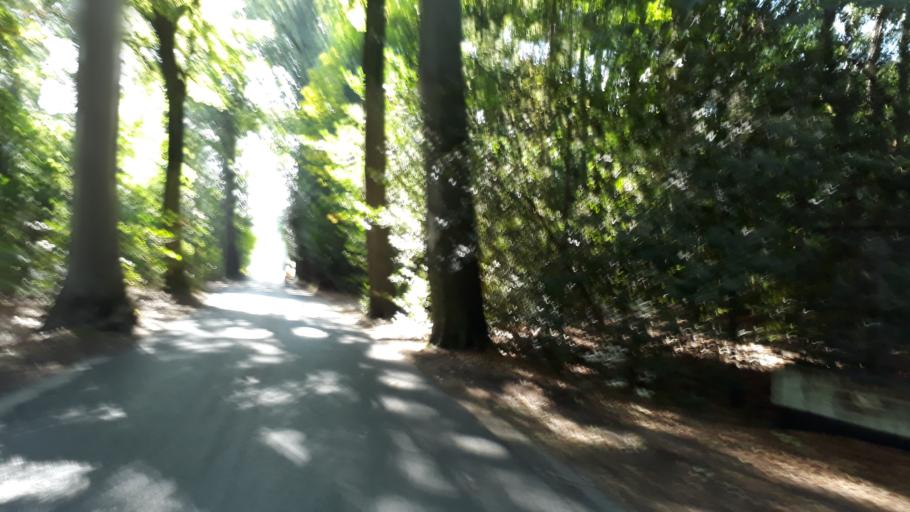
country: BE
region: Flanders
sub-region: Provincie West-Vlaanderen
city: Torhout
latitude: 51.0734
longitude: 3.1331
